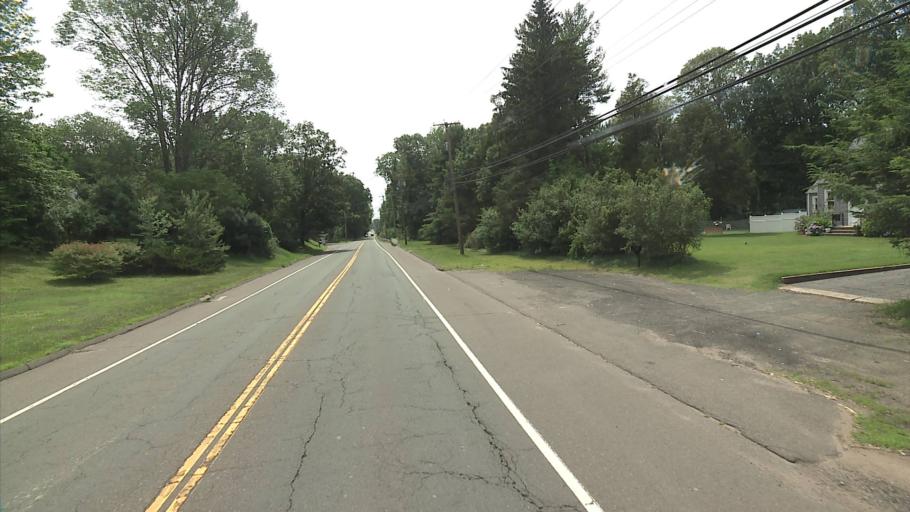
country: US
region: Connecticut
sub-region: New Haven County
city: North Branford
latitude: 41.3393
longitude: -72.7519
